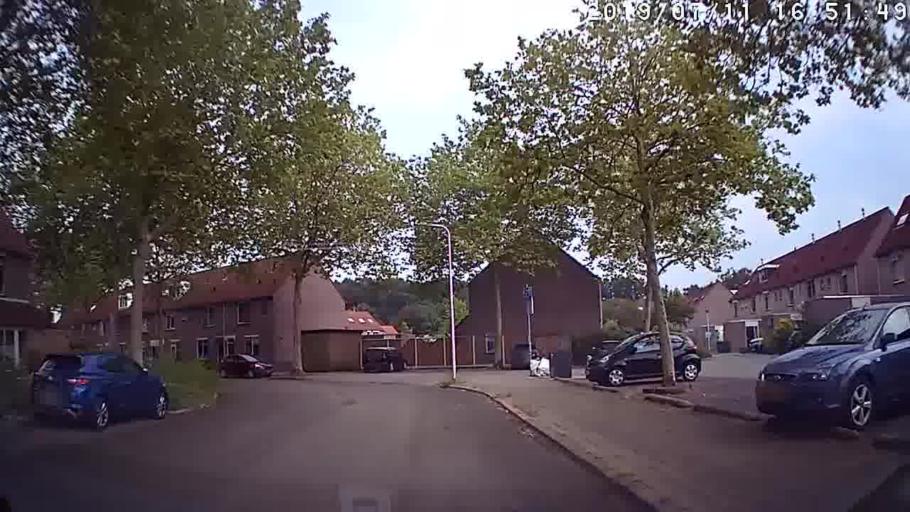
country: NL
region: Overijssel
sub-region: Gemeente Zwolle
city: Zwolle
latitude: 52.4830
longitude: 6.1194
